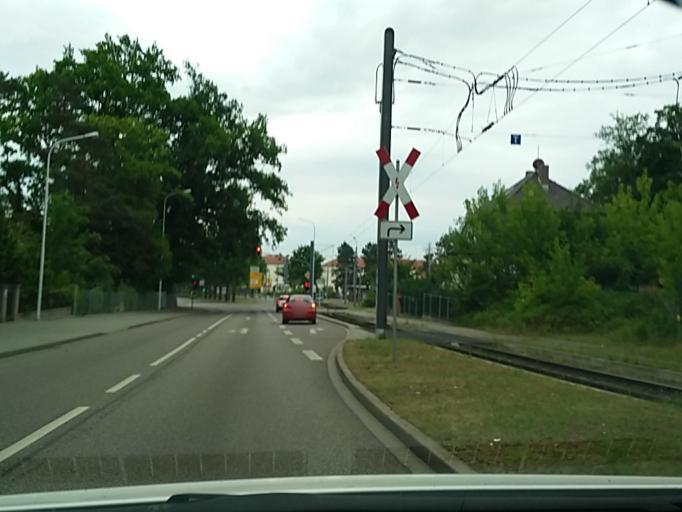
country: DE
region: Saxony-Anhalt
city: Halle Neustadt
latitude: 51.5019
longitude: 11.9311
